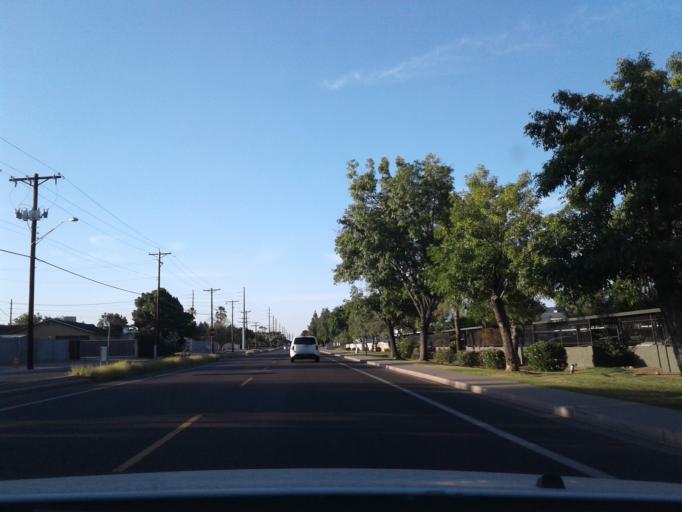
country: US
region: Arizona
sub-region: Maricopa County
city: Glendale
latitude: 33.5614
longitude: -112.1082
